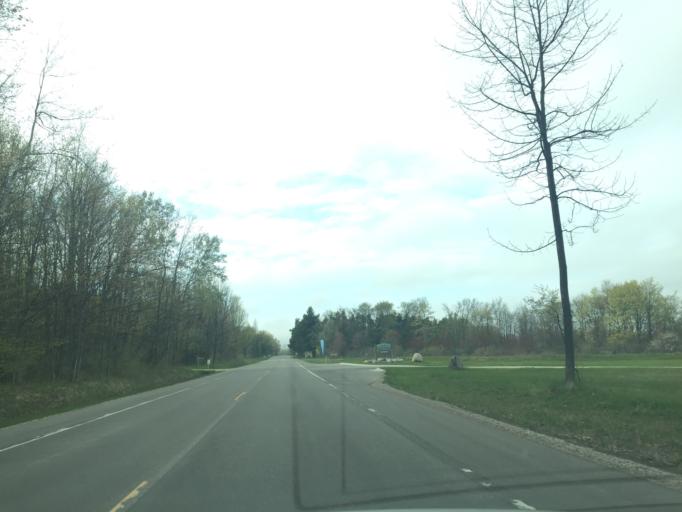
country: US
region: Michigan
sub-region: Leelanau County
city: Leland
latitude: 45.0765
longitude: -85.5907
